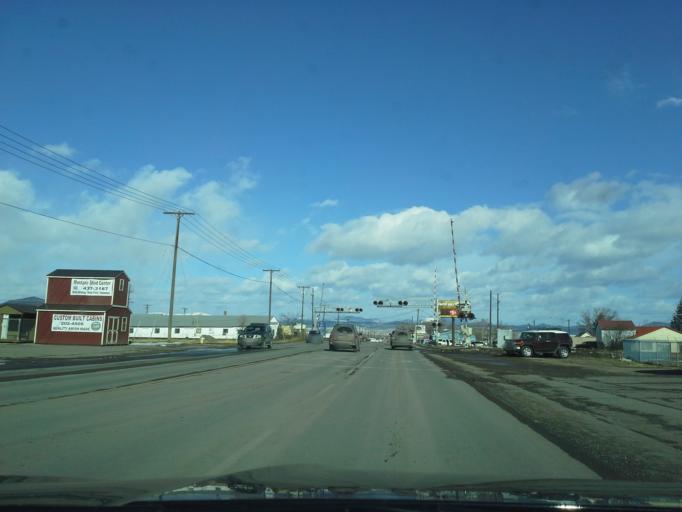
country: US
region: Montana
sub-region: Lewis and Clark County
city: Helena
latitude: 46.6000
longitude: -112.0205
